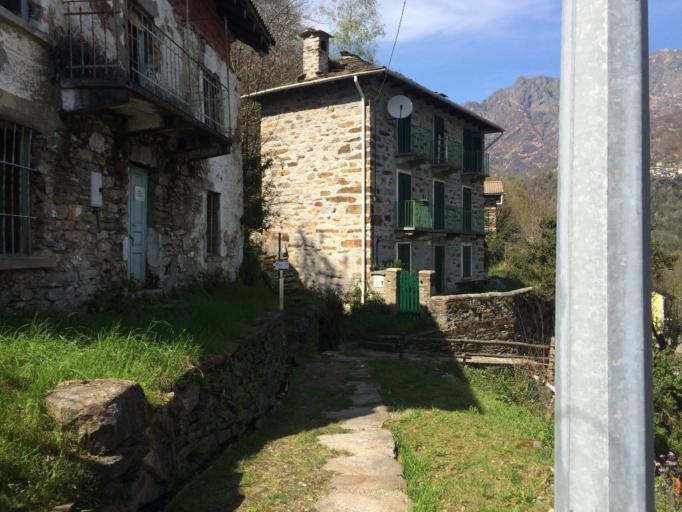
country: IT
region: Piedmont
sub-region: Provincia Verbano-Cusio-Ossola
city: Falmenta
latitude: 46.0801
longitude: 8.5953
